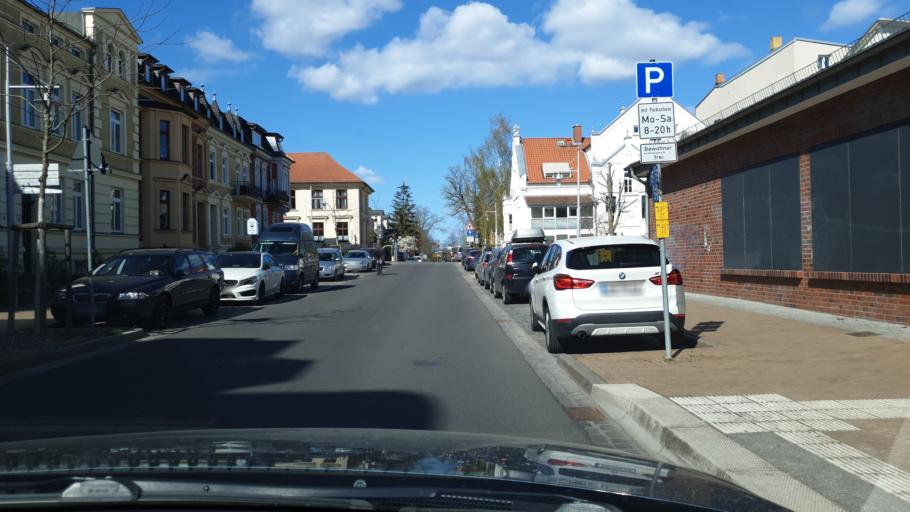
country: DE
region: Mecklenburg-Vorpommern
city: Schelfstadt
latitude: 53.6346
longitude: 11.4182
